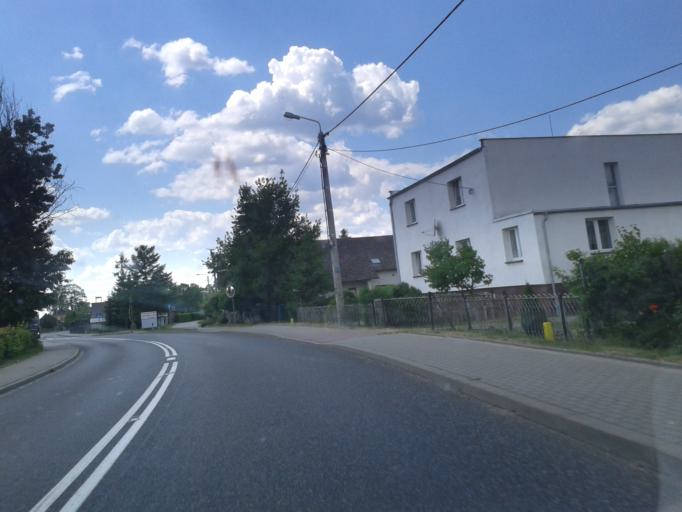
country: PL
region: Pomeranian Voivodeship
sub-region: Powiat czluchowski
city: Debrzno
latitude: 53.5734
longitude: 17.0789
